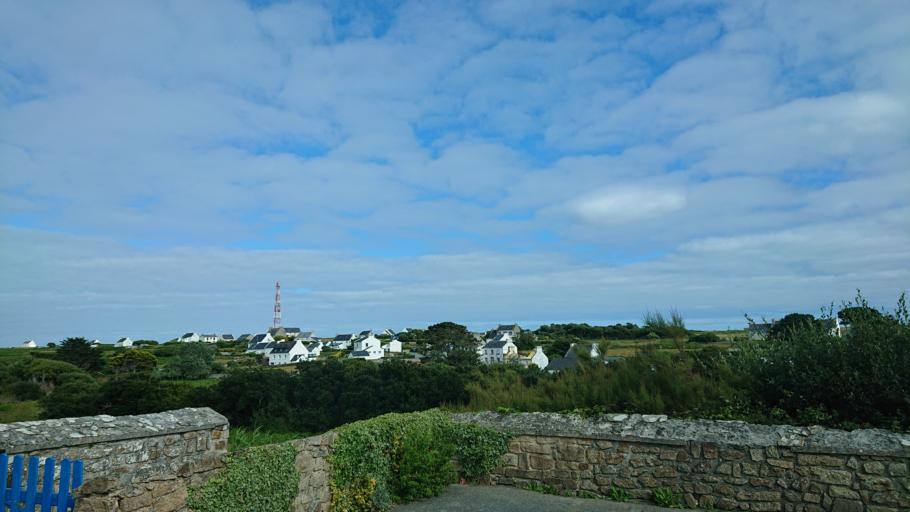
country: FR
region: Brittany
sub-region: Departement du Finistere
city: Porspoder
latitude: 48.4576
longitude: -5.0952
